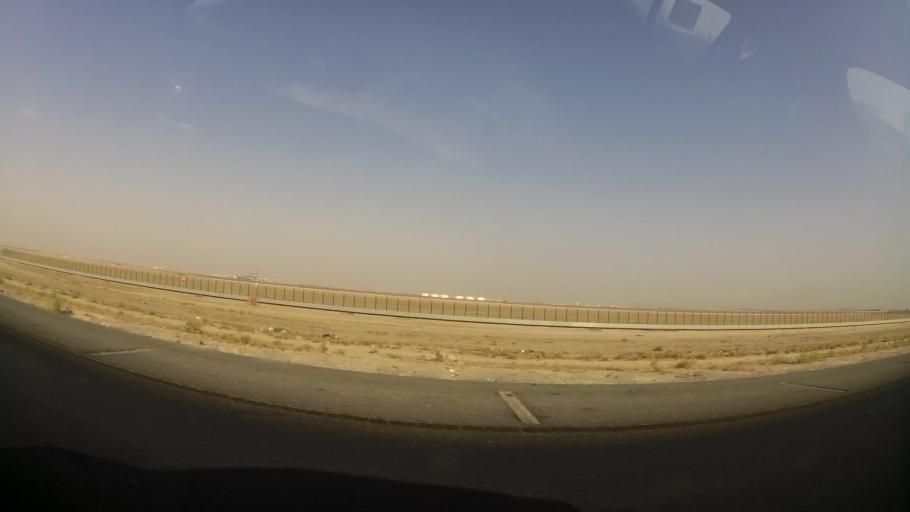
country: KW
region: Al Farwaniyah
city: Janub as Surrah
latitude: 29.1907
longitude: 48.0015
